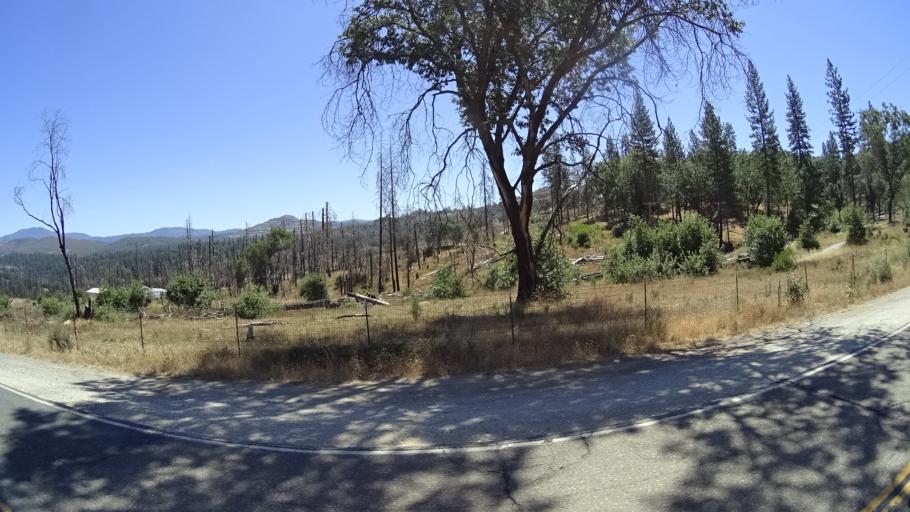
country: US
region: California
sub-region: Calaveras County
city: Mountain Ranch
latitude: 38.2624
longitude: -120.5119
